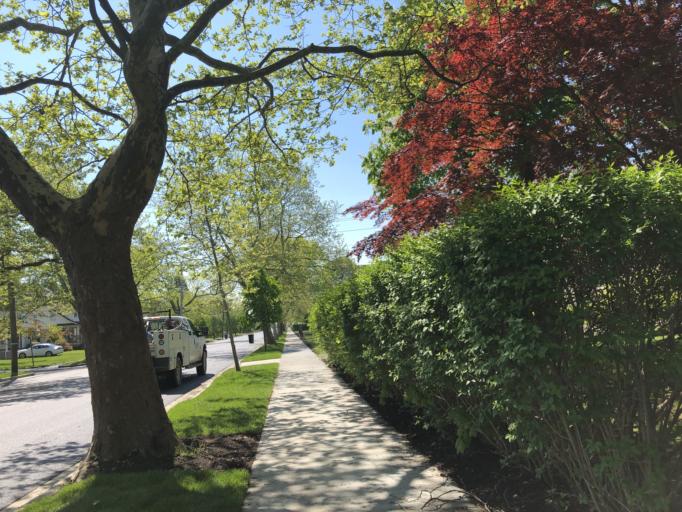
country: US
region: New York
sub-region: Suffolk County
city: Bay Shore
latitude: 40.7197
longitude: -73.2459
